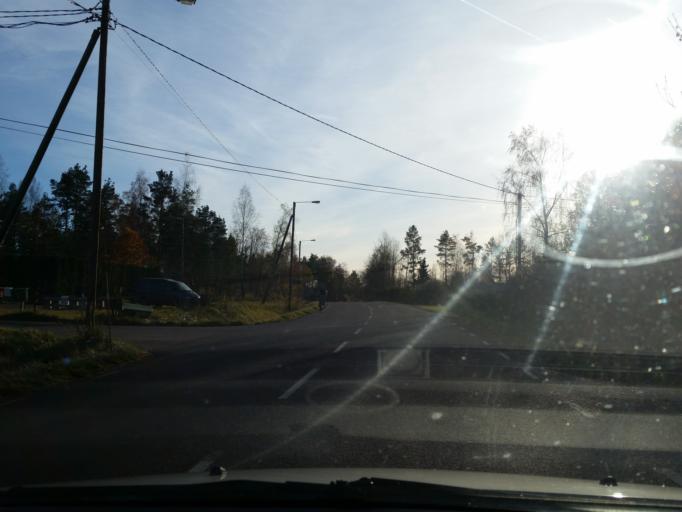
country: AX
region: Alands landsbygd
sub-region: Jomala
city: Jomala
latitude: 60.1350
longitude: 19.9384
